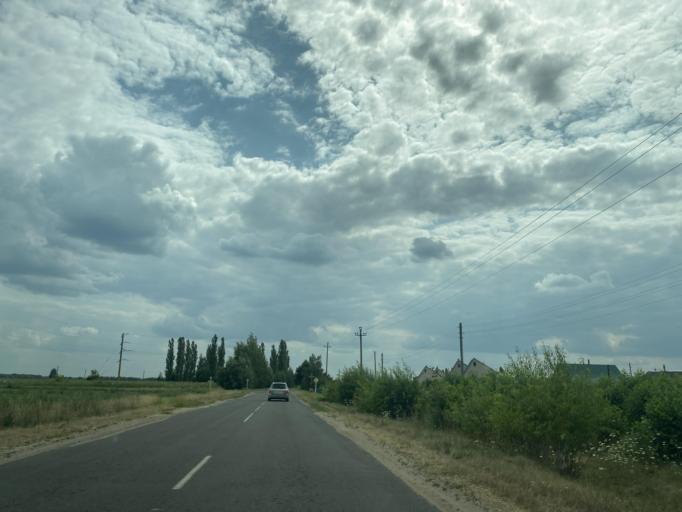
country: BY
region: Brest
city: Ivanava
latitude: 52.3503
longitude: 25.6293
